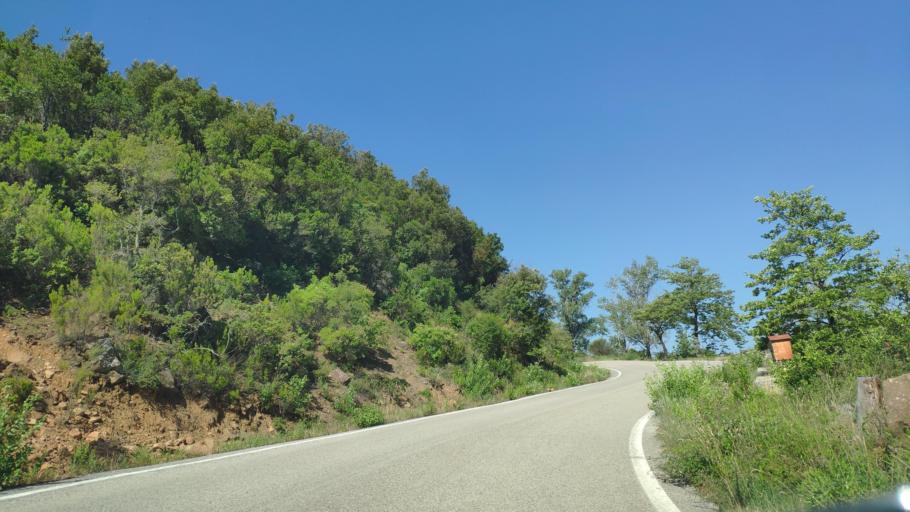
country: GR
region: West Greece
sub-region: Nomos Aitolias kai Akarnanias
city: Sardinia
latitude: 38.9268
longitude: 21.4107
